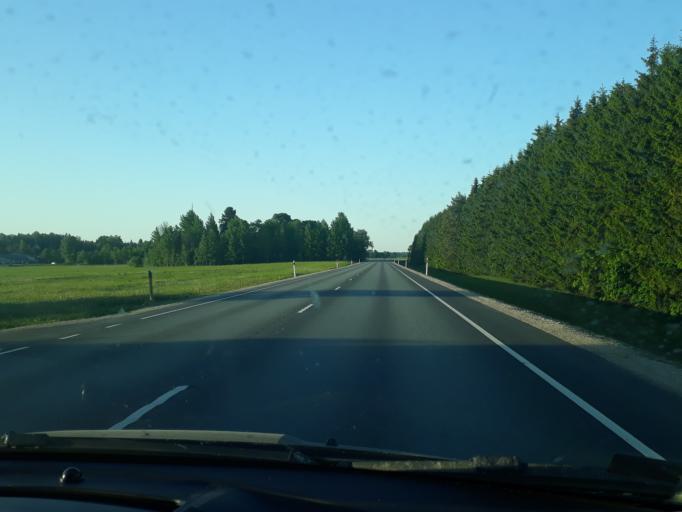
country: EE
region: Paernumaa
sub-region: Tootsi vald
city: Tootsi
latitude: 58.5404
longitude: 24.8402
